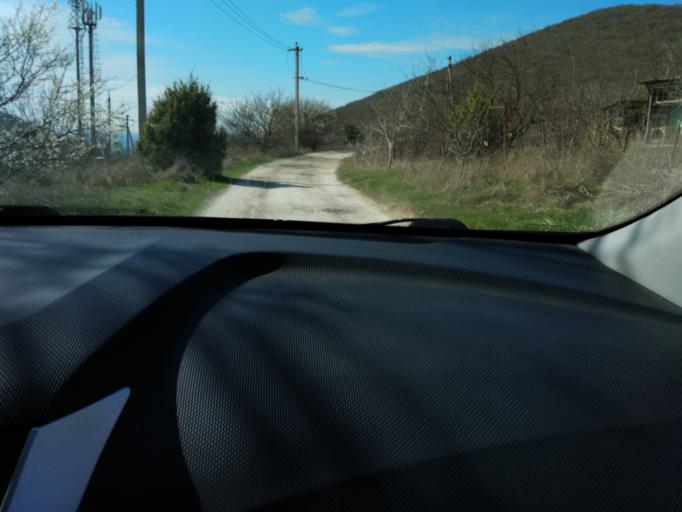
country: RU
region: Krasnodarskiy
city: Myskhako
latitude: 44.6801
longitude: 37.7089
